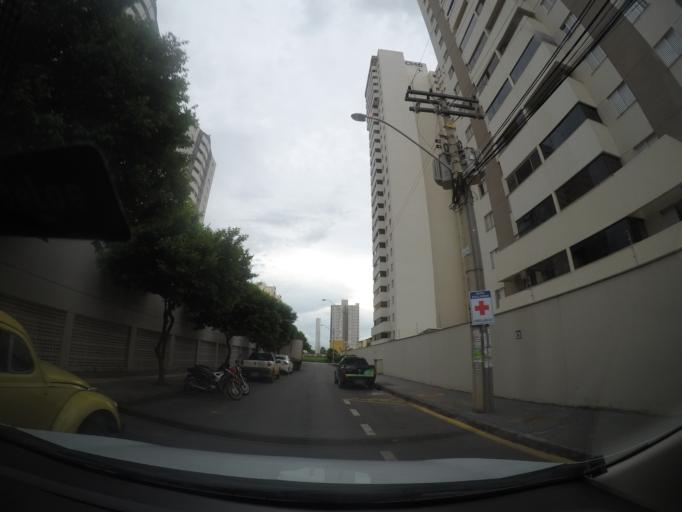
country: BR
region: Goias
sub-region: Goiania
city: Goiania
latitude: -16.6536
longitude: -49.2428
